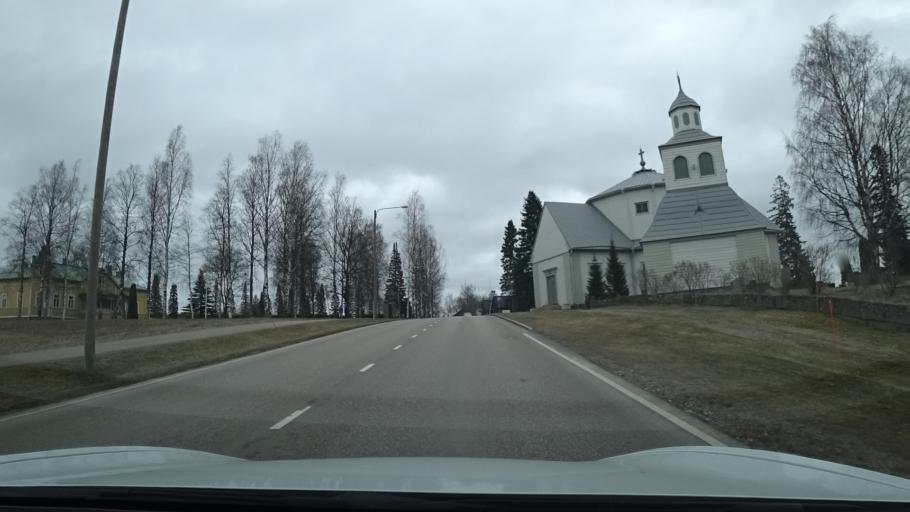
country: FI
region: Uusimaa
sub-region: Porvoo
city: Myrskylae
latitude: 60.6664
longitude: 25.8500
